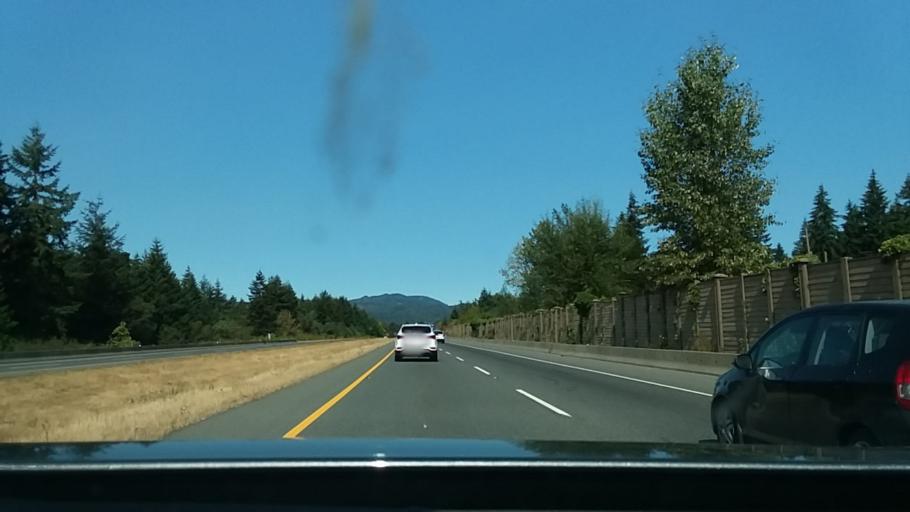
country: CA
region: British Columbia
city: Nanaimo
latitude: 49.1931
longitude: -124.0144
